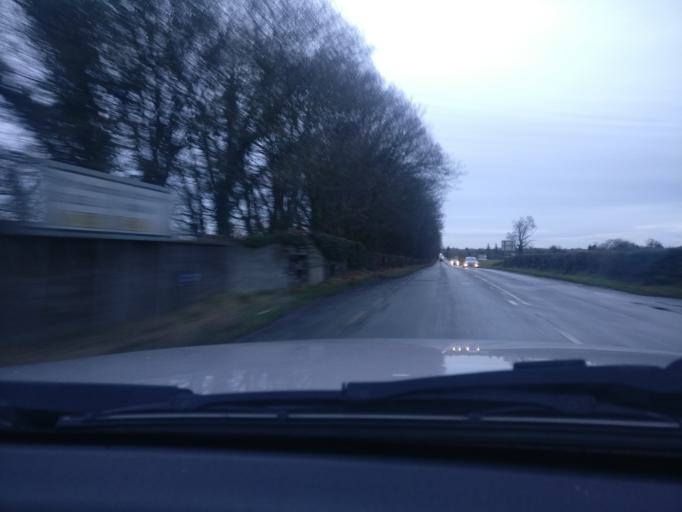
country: IE
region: Leinster
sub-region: An Mhi
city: Navan
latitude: 53.6817
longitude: -6.7588
